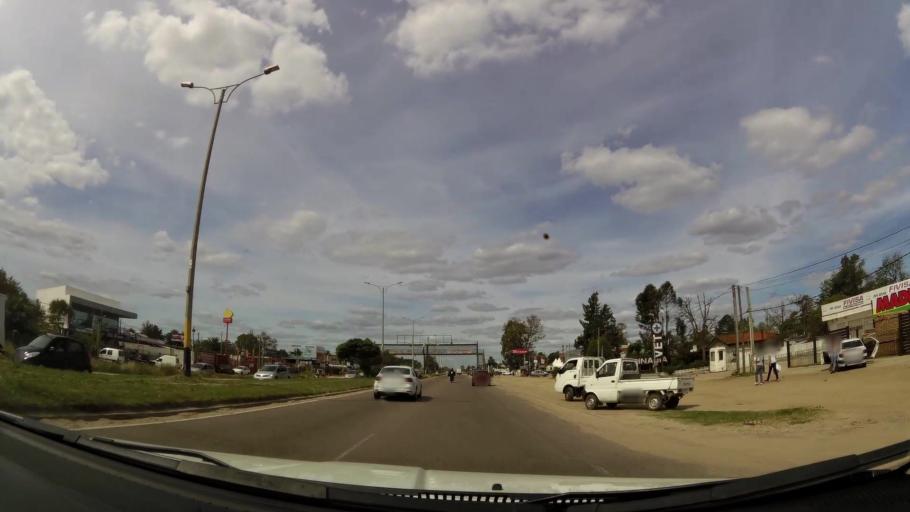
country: UY
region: Canelones
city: Colonia Nicolich
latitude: -34.8265
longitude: -55.9666
